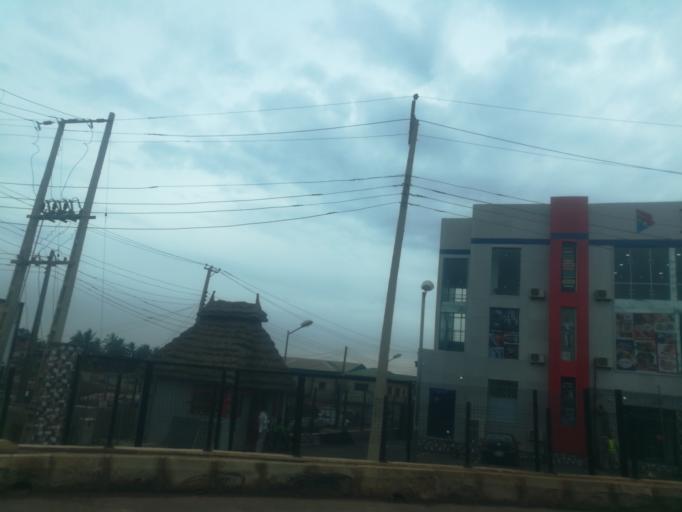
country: NG
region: Oyo
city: Ibadan
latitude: 7.3904
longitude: 3.9424
